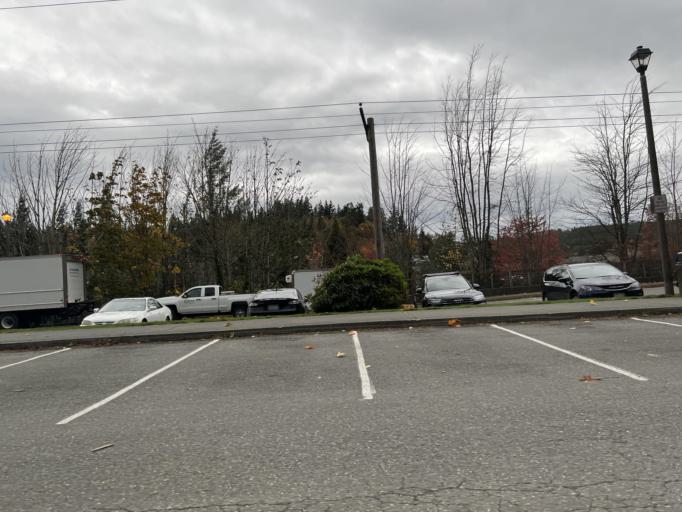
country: US
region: Washington
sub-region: King County
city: Snoqualmie
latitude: 47.5426
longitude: -121.8355
